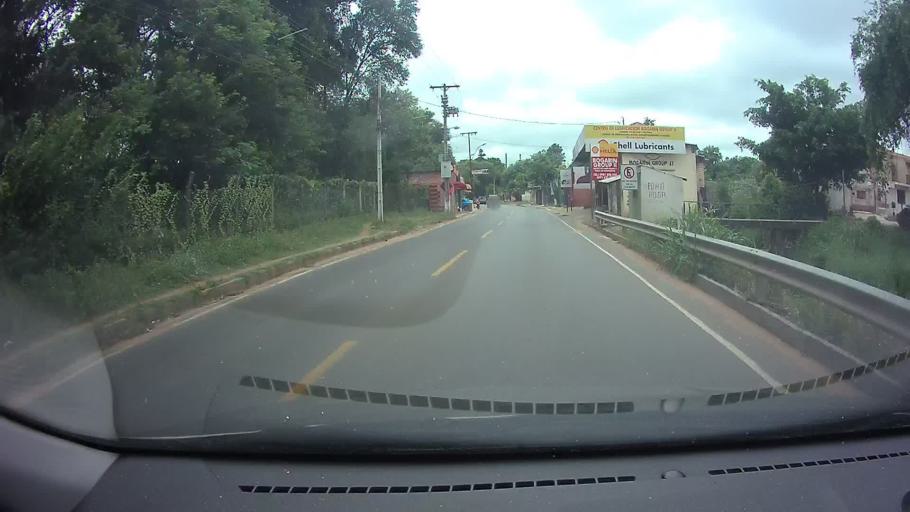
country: PY
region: Central
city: Nemby
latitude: -25.3796
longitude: -57.5461
